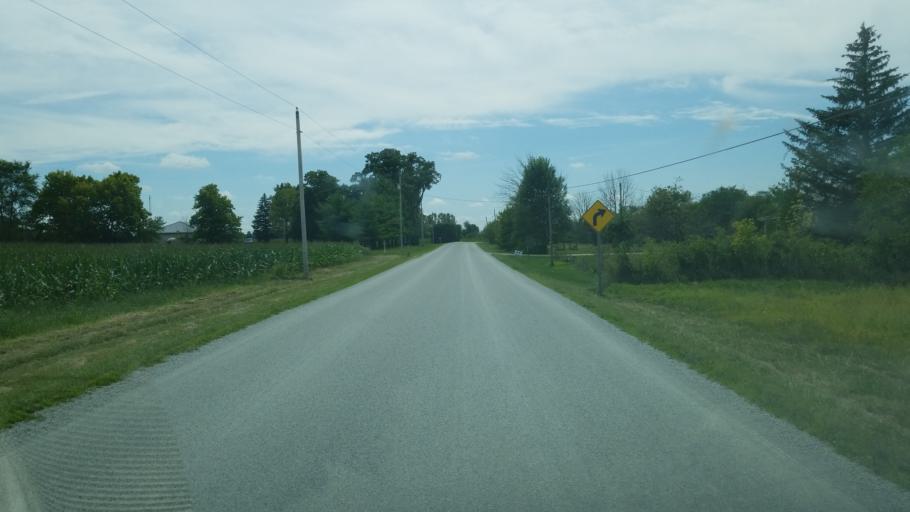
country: US
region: Ohio
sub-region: Hardin County
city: Kenton
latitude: 40.5748
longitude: -83.5051
